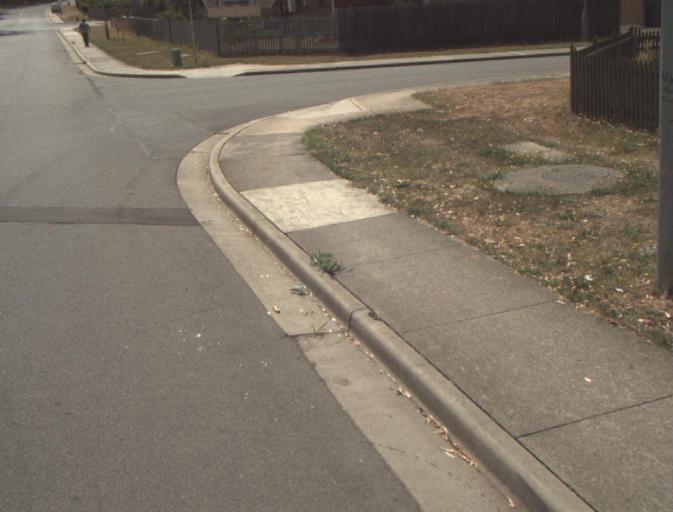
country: AU
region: Tasmania
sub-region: Launceston
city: Newstead
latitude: -41.4163
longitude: 147.1790
